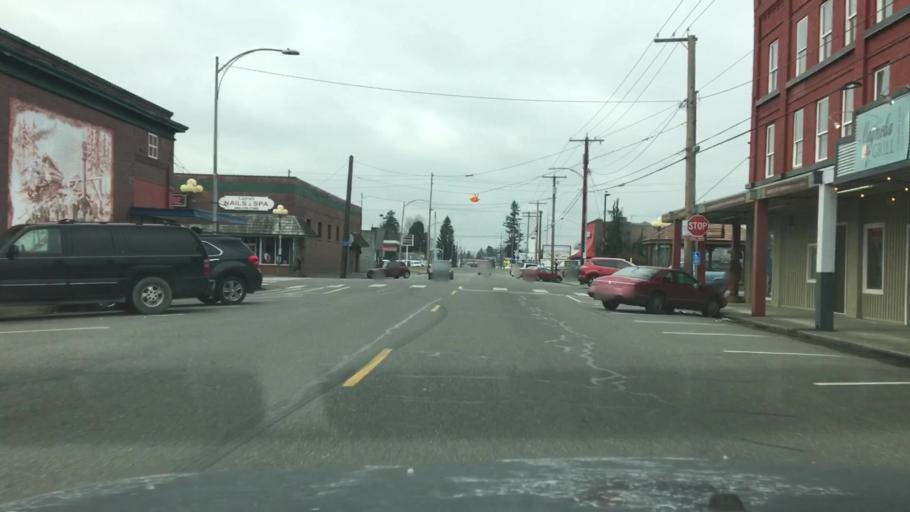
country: US
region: Washington
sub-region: Skagit County
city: Sedro-Woolley
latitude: 48.5054
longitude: -122.2379
